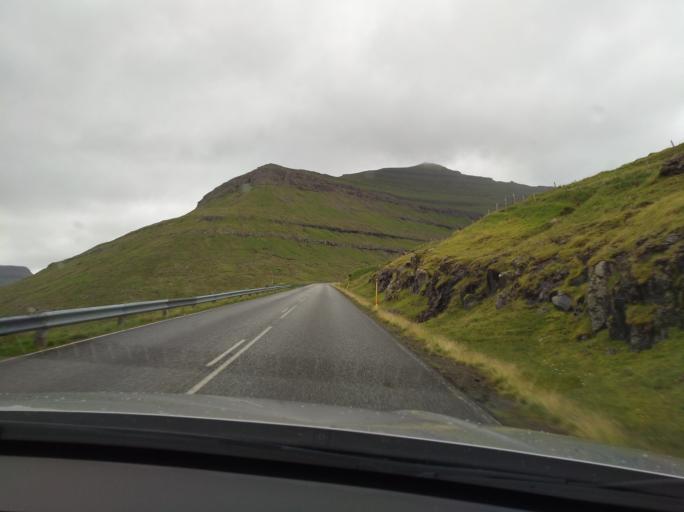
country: FO
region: Eysturoy
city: Fuglafjordur
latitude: 62.2221
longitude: -6.8754
